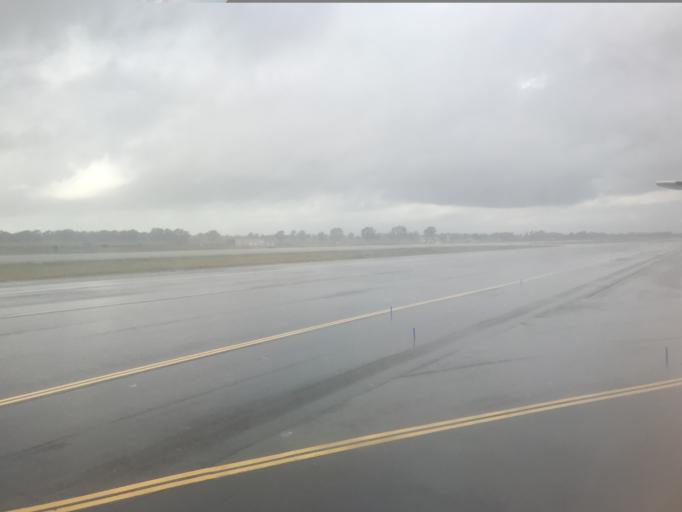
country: IT
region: Latium
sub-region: Citta metropolitana di Roma Capitale
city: Npp 23 (Parco Leonardo)
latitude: 41.8243
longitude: 12.2680
